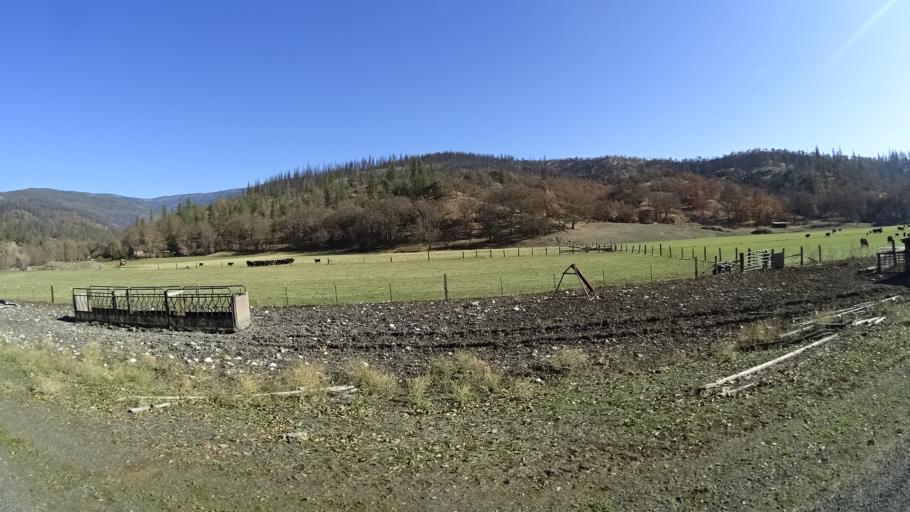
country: US
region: California
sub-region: Siskiyou County
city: Happy Camp
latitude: 41.8325
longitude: -123.0081
